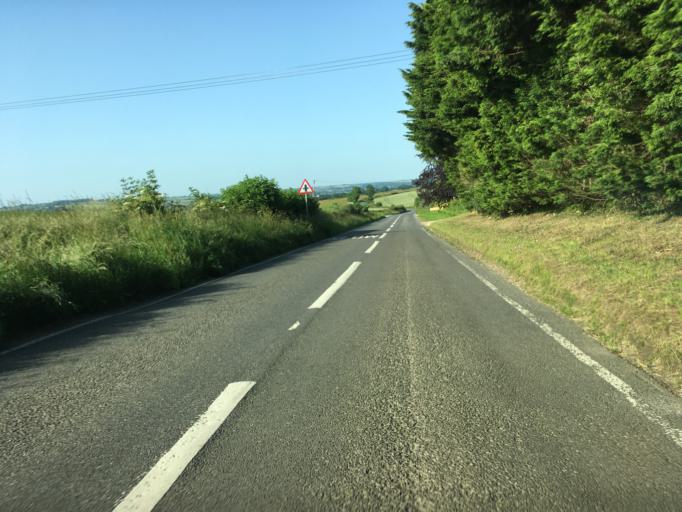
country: GB
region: England
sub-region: Oxfordshire
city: Shipton under Wychwood
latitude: 51.8482
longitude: -1.5833
